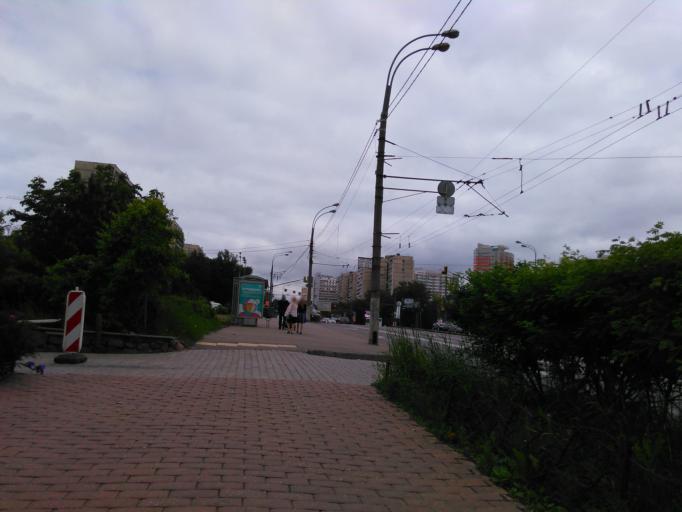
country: RU
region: Moscow
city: Troparevo
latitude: 55.6700
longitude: 37.4939
